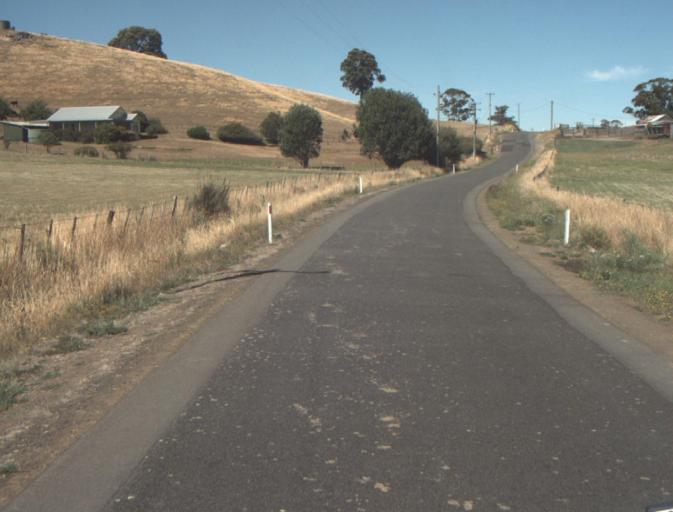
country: AU
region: Tasmania
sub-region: Launceston
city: Newstead
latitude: -41.3427
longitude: 147.3035
